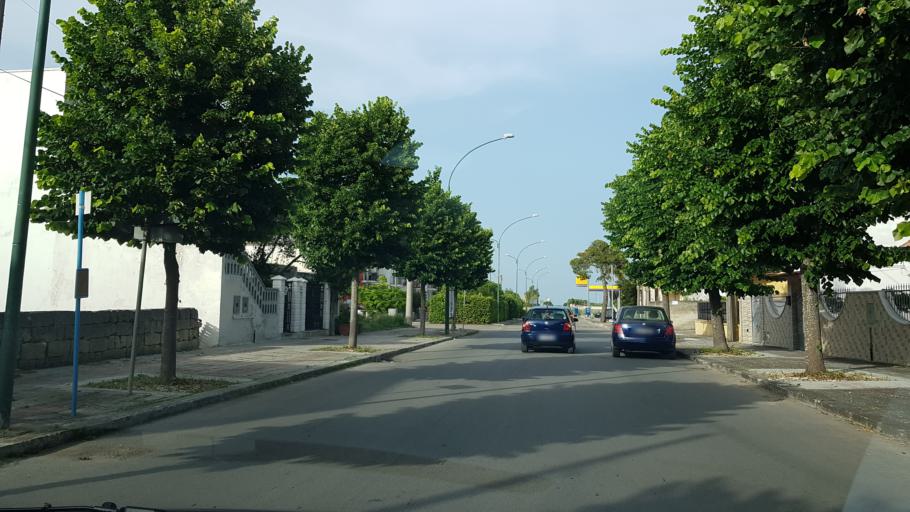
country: IT
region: Apulia
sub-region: Provincia di Brindisi
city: San Pancrazio Salentino
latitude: 40.4209
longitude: 17.8479
